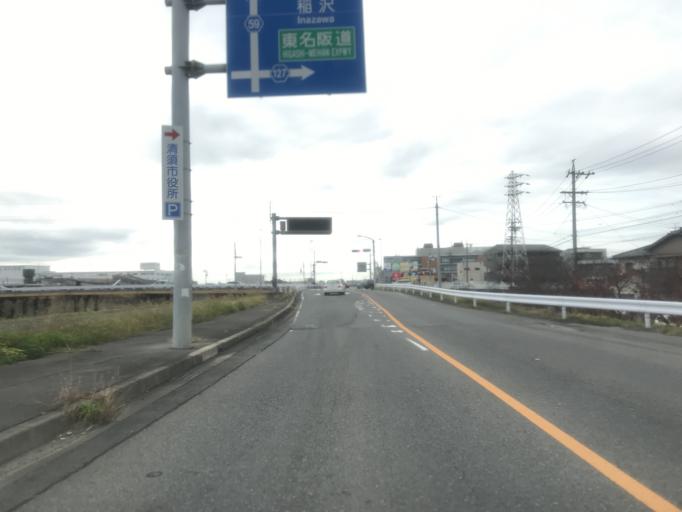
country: JP
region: Aichi
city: Nagoya-shi
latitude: 35.2023
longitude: 136.8551
